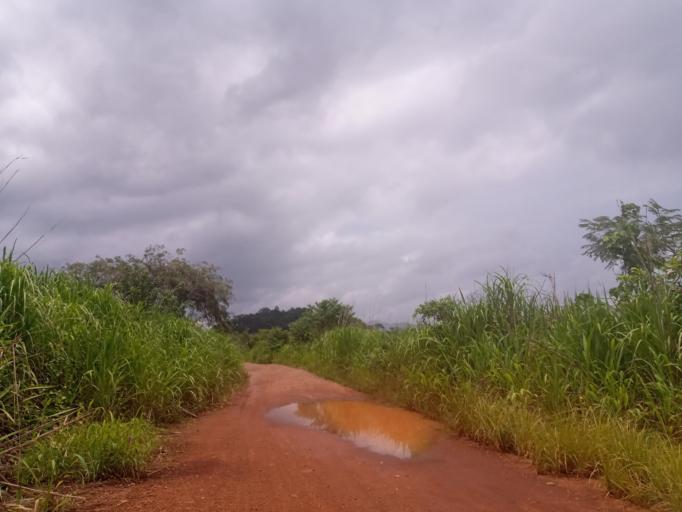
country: SL
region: Northern Province
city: Bumbuna
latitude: 8.9715
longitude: -11.7547
